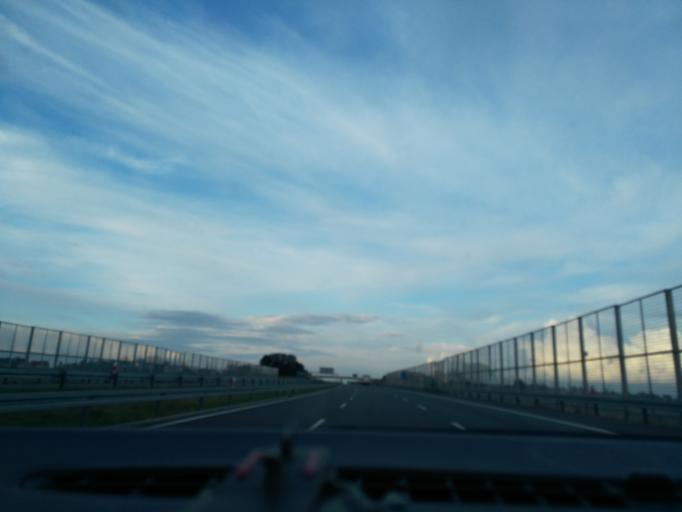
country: PL
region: Lublin Voivodeship
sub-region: Powiat lubelski
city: Lublin
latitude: 51.2978
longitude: 22.5310
